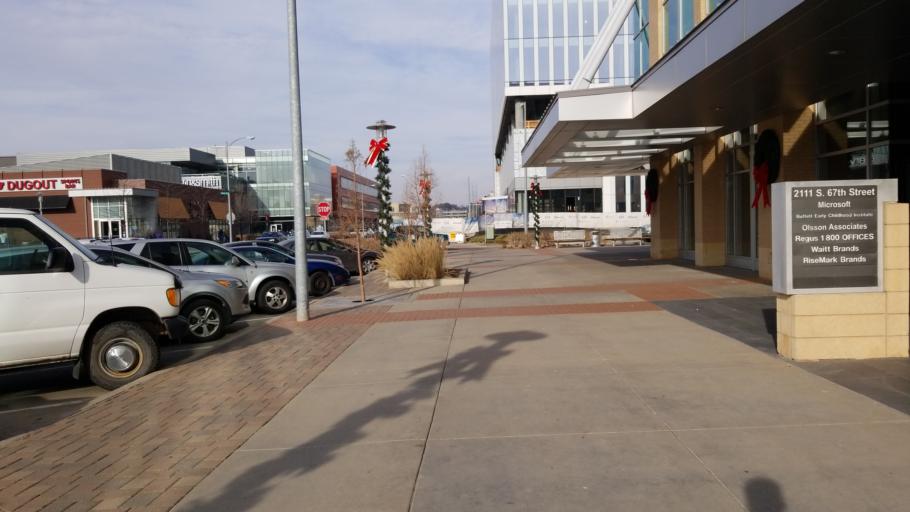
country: US
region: Nebraska
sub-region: Douglas County
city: Ralston
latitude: 41.2394
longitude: -96.0145
